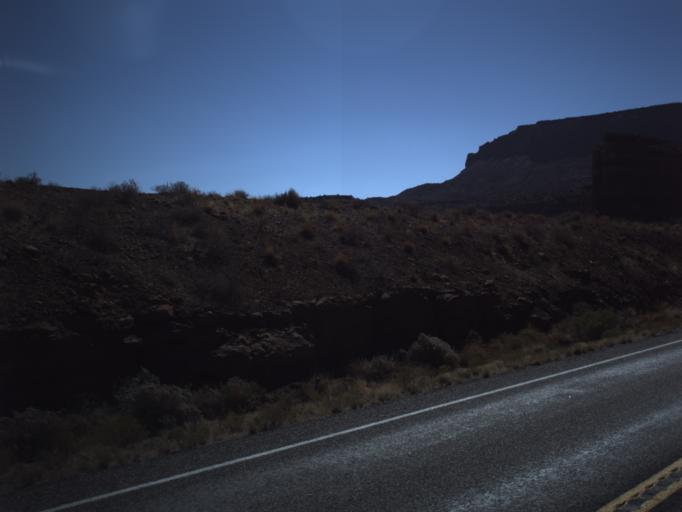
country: US
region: Utah
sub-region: San Juan County
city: Blanding
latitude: 37.7469
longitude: -110.2806
